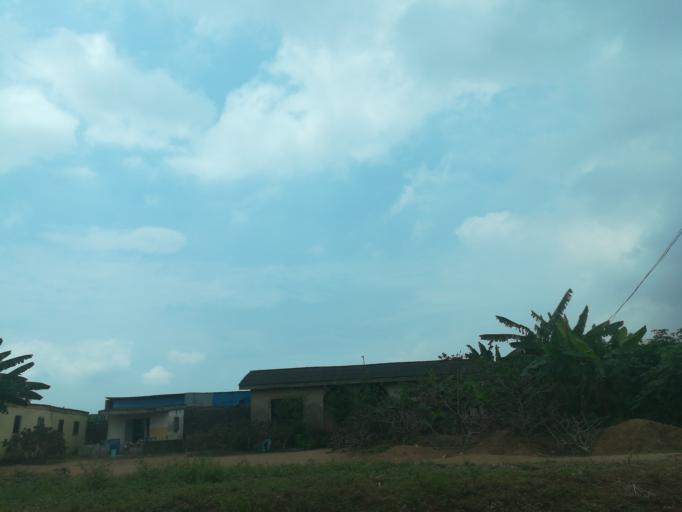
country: NG
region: Lagos
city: Ikorodu
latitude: 6.6178
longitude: 3.5206
